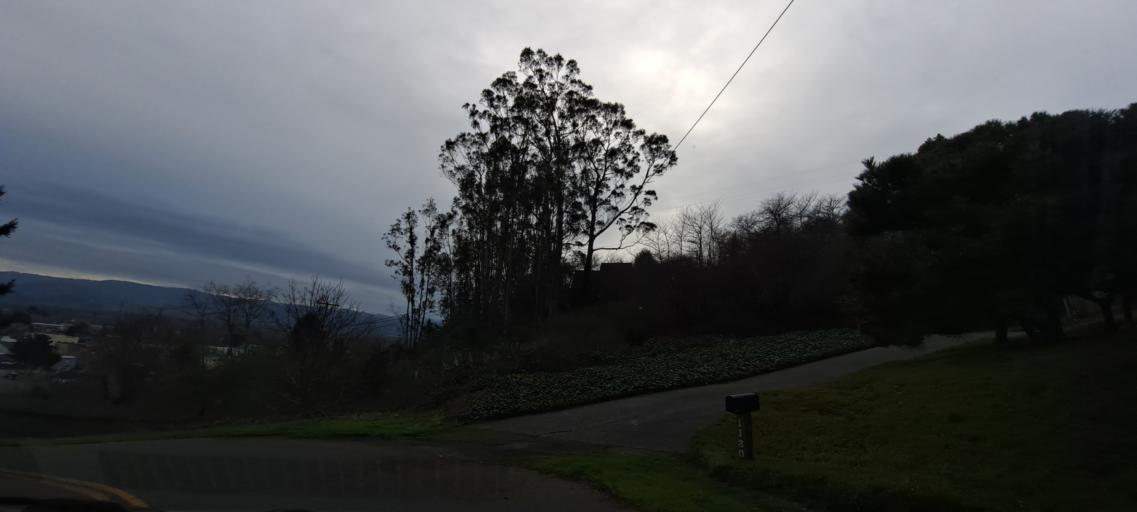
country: US
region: California
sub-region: Humboldt County
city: Fortuna
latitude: 40.6017
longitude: -124.1549
